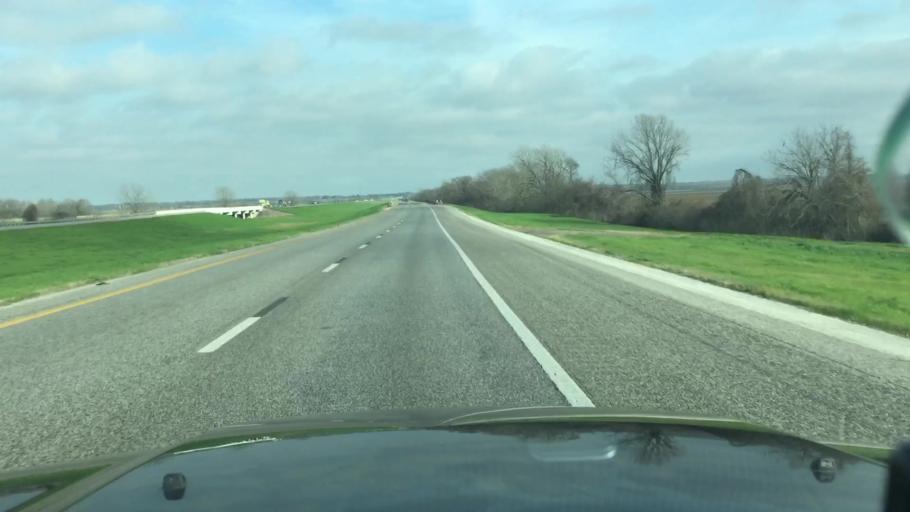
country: US
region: Texas
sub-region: Waller County
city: Hempstead
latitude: 30.1296
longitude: -96.1802
